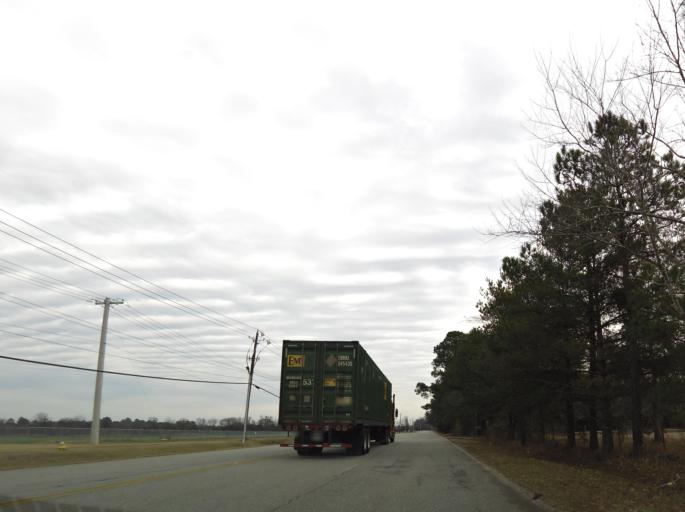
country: US
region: Georgia
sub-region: Houston County
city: Warner Robins
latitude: 32.6834
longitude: -83.6389
